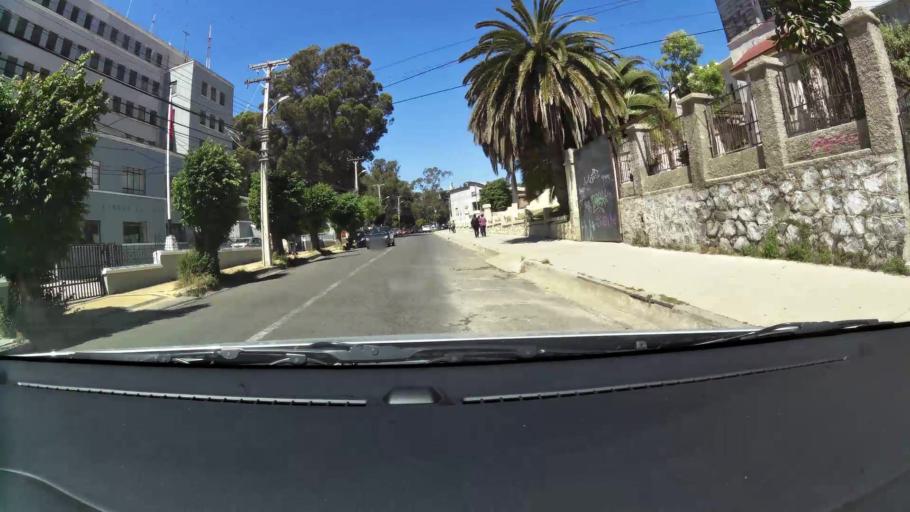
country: CL
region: Valparaiso
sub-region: Provincia de Valparaiso
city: Valparaiso
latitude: -33.0267
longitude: -71.6370
